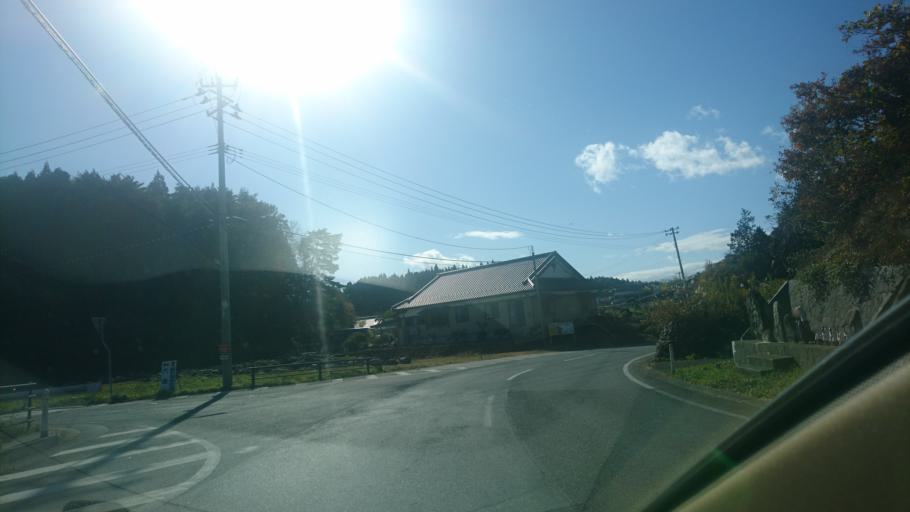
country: JP
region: Iwate
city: Ofunato
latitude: 38.9944
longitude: 141.7264
